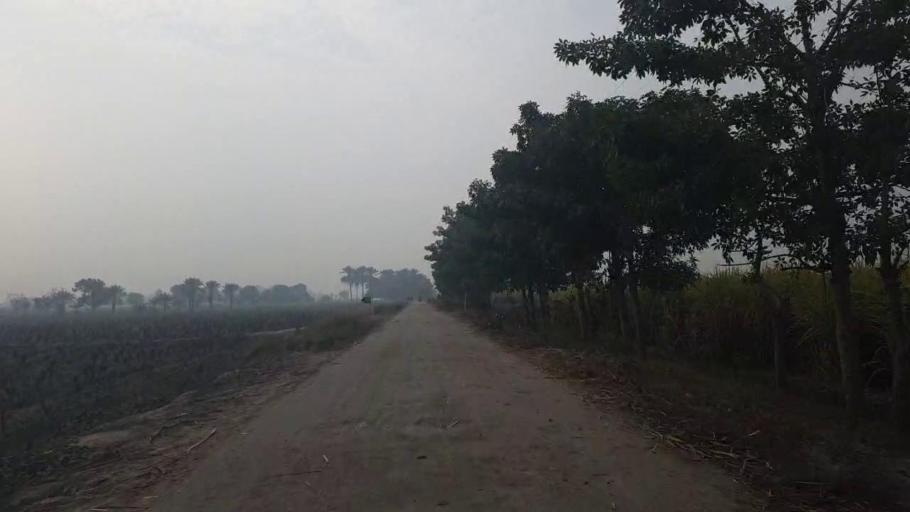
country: PK
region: Sindh
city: Tando Adam
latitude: 25.7176
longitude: 68.6804
